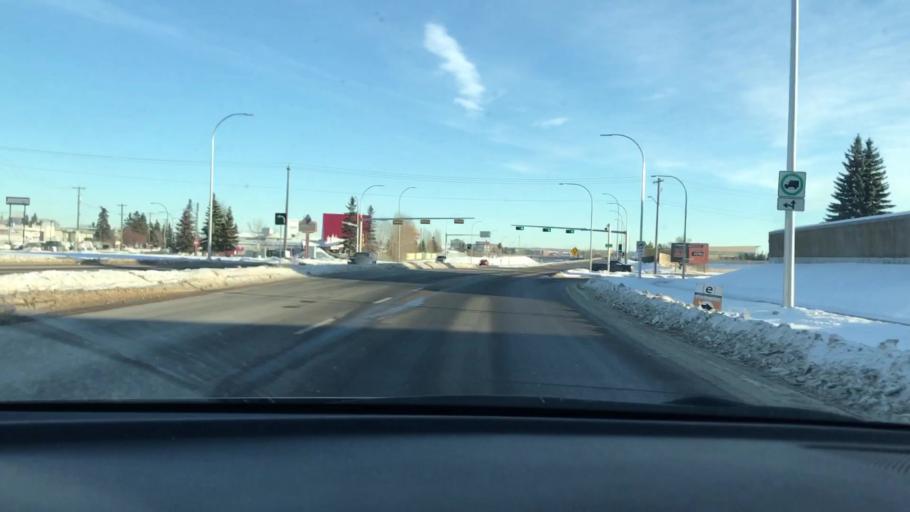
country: CA
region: Alberta
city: Edmonton
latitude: 53.5178
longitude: -113.4383
